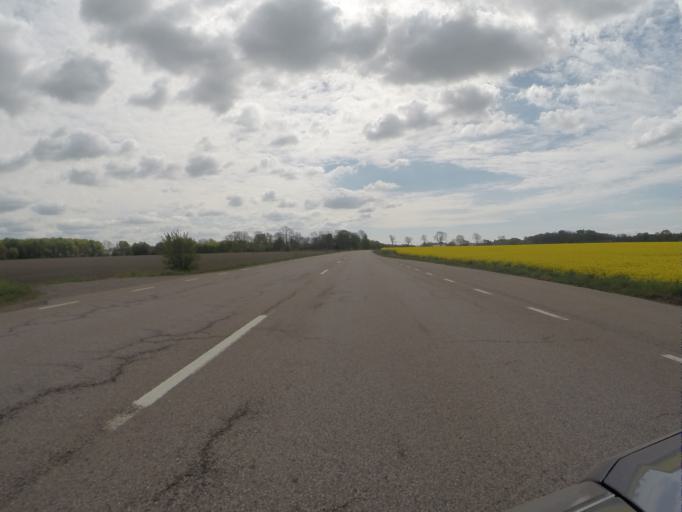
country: SE
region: Skane
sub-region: Helsingborg
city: Hyllinge
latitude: 56.0956
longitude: 12.8030
